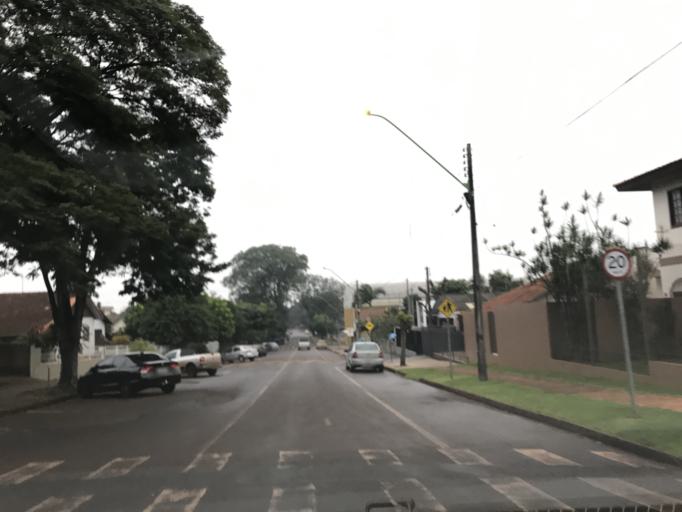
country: BR
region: Parana
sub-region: Palotina
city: Palotina
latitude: -24.2820
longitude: -53.8440
